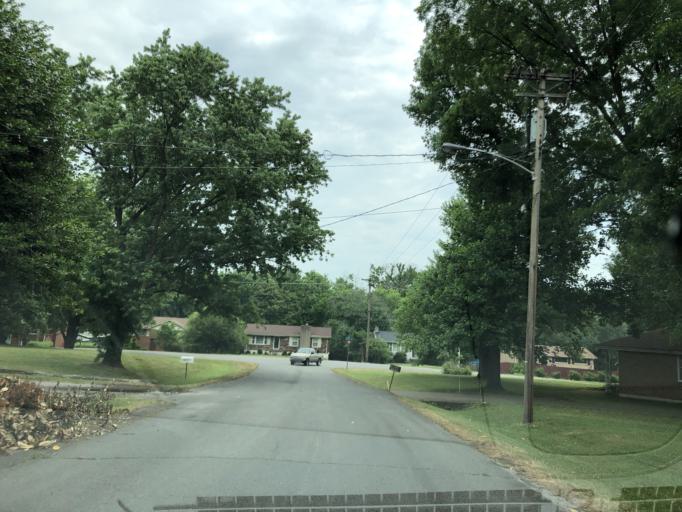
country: US
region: Tennessee
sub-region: Davidson County
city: Oak Hill
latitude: 36.0668
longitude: -86.6787
